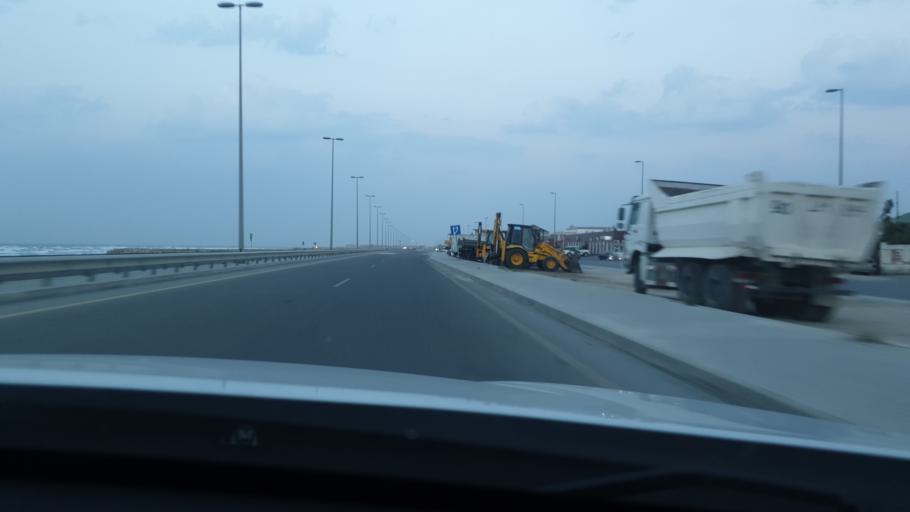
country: AZ
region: Baki
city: Bilajer
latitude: 40.5870
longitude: 50.0382
